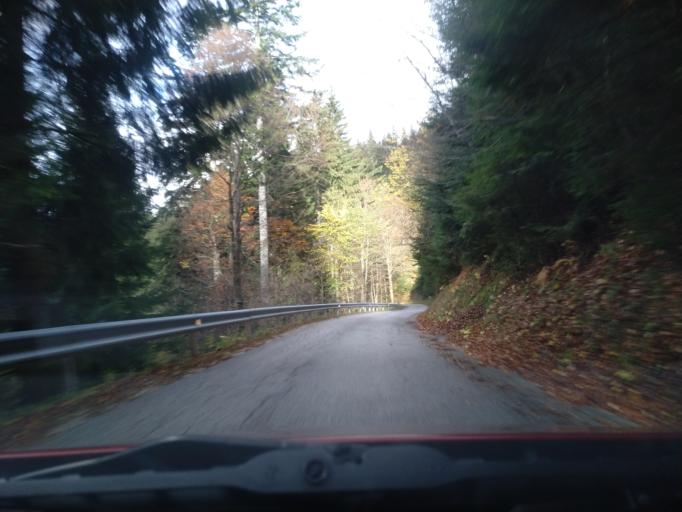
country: SI
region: Luce
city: Luce
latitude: 46.2912
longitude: 14.6972
